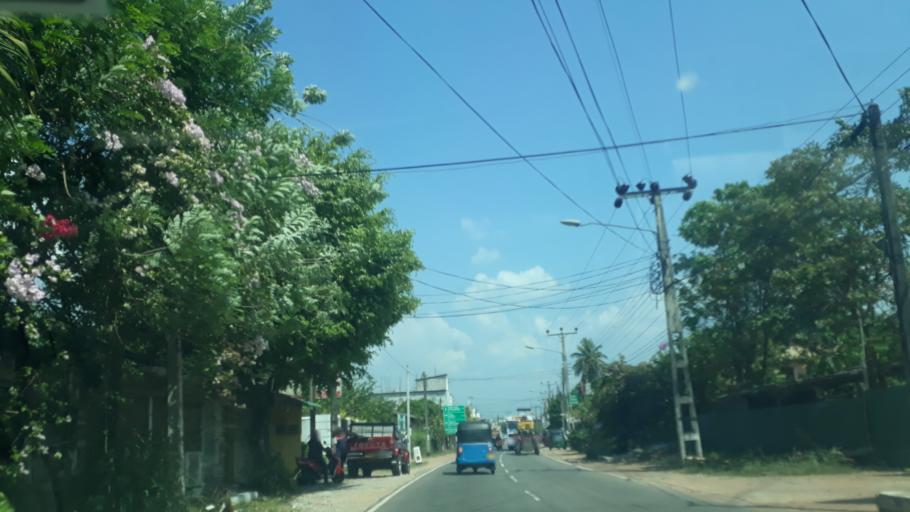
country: LK
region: Western
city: Gampaha
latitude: 7.0930
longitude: 79.9881
